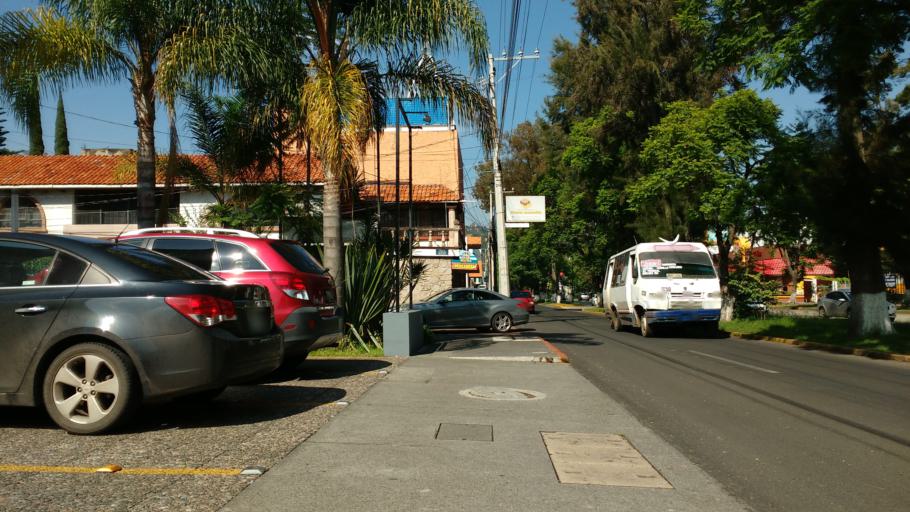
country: MX
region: Michoacan
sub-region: Morelia
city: Montana Monarca (Punta Altozano)
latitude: 19.6856
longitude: -101.1636
